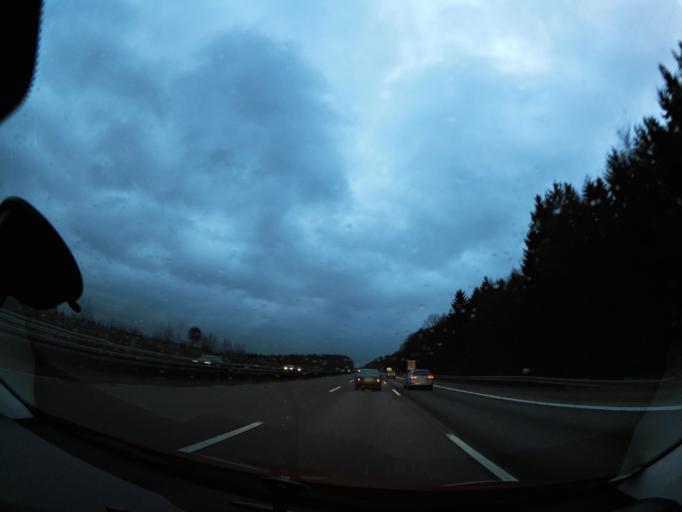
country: DE
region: Rheinland-Pfalz
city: Gorgeshausen
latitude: 50.4126
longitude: 7.9672
